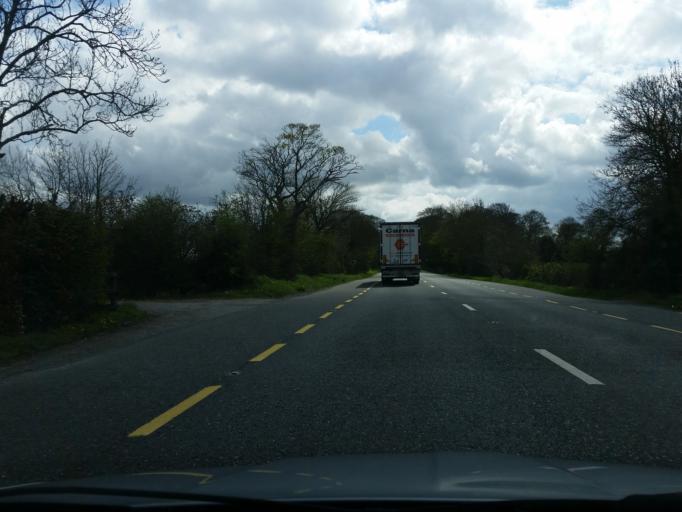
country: IE
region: Leinster
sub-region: An Mhi
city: Ashbourne
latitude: 53.5350
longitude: -6.4231
